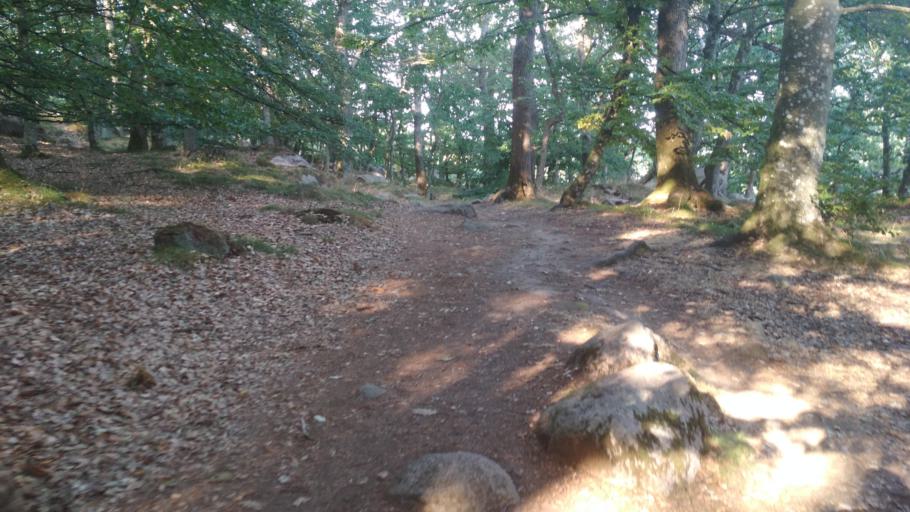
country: DK
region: Capital Region
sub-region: Bornholm Kommune
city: Akirkeby
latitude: 55.1086
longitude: 14.8987
